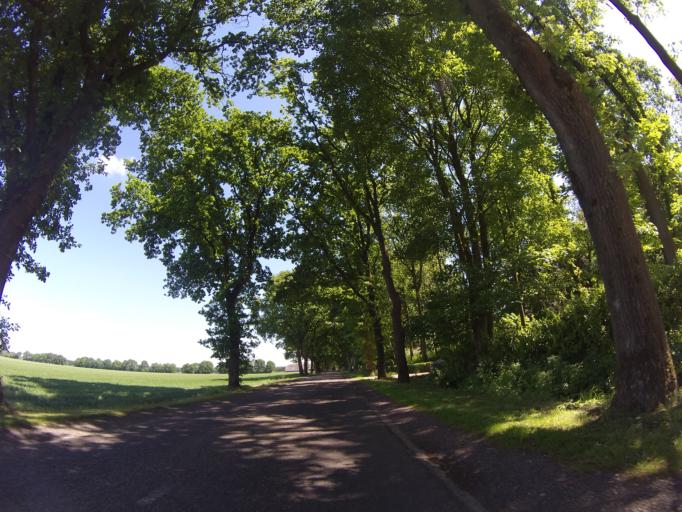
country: NL
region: Drenthe
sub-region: Gemeente Hoogeveen
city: Hoogeveen
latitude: 52.7911
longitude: 6.5648
